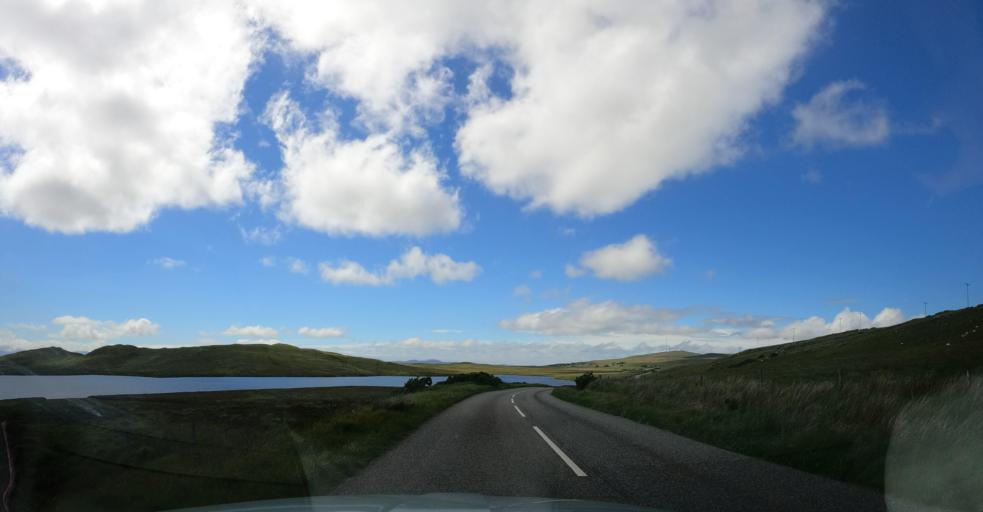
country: GB
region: Scotland
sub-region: Eilean Siar
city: Stornoway
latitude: 58.1584
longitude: -6.5269
